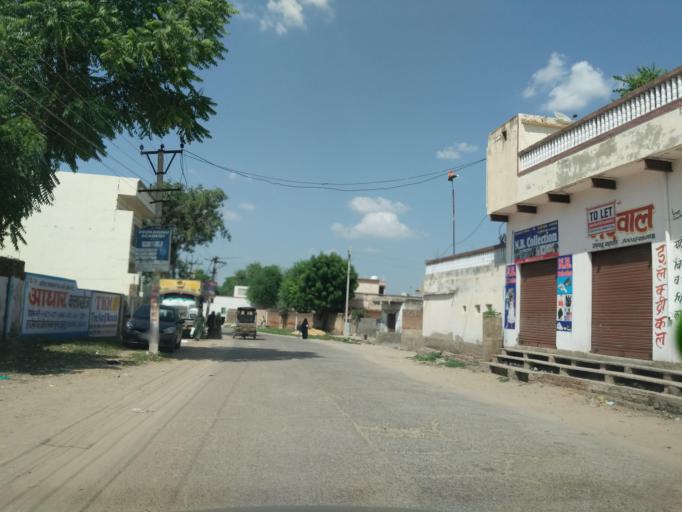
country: IN
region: Rajasthan
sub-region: Jhunjhunun
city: Jhunjhunun
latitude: 28.1360
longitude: 75.3919
